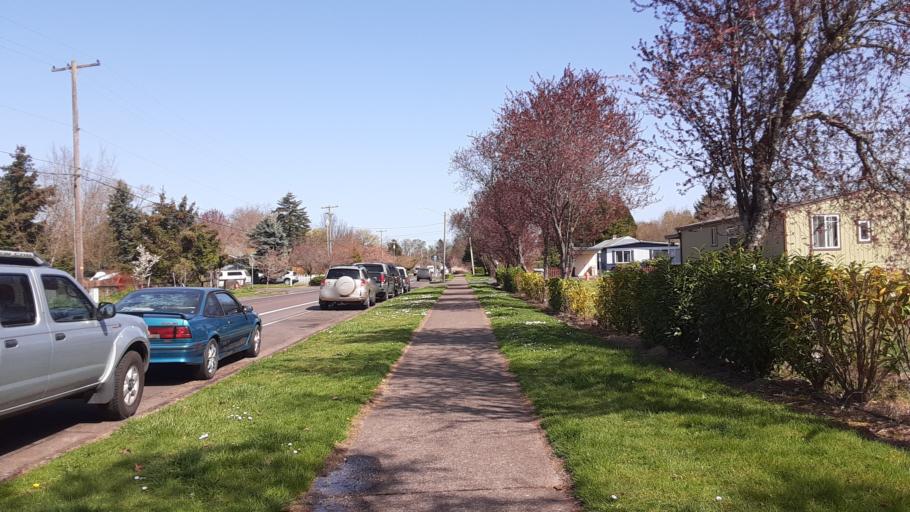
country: US
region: Oregon
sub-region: Benton County
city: Corvallis
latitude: 44.5367
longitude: -123.2632
